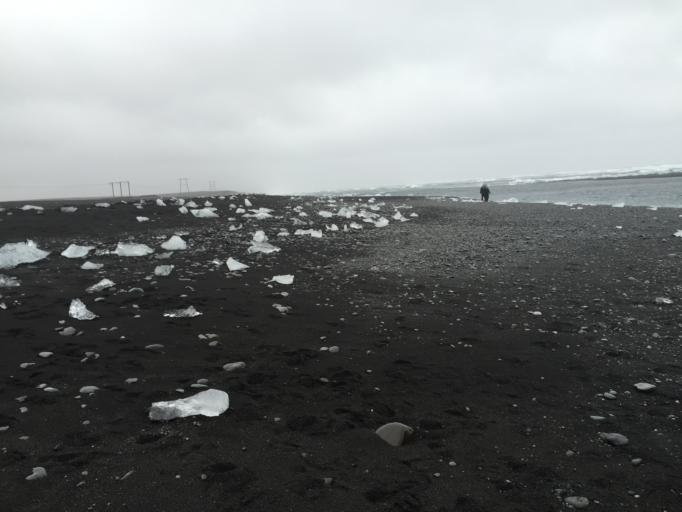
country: IS
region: East
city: Hoefn
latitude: 64.0436
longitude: -16.1759
